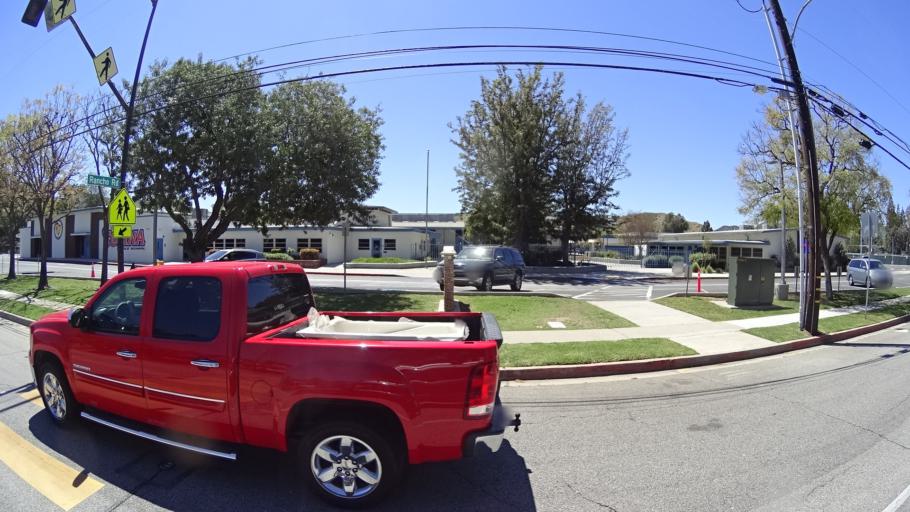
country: US
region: California
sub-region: Ventura County
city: Thousand Oaks
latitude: 34.1826
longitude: -118.8516
